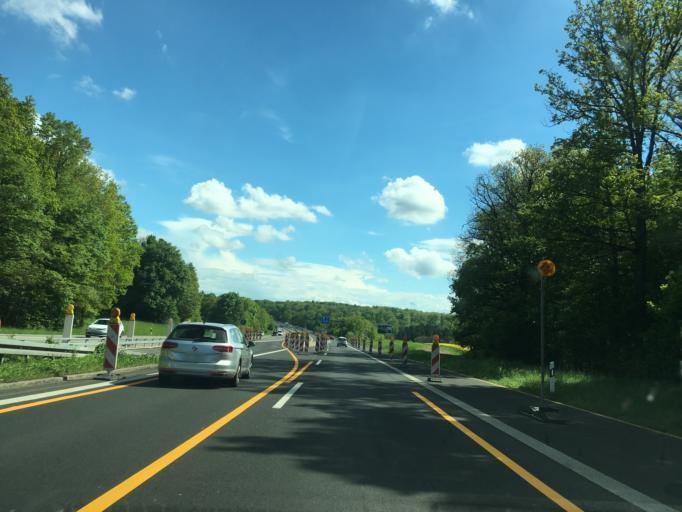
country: DE
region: Bavaria
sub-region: Regierungsbezirk Unterfranken
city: Rimpar
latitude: 49.8653
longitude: 9.9923
